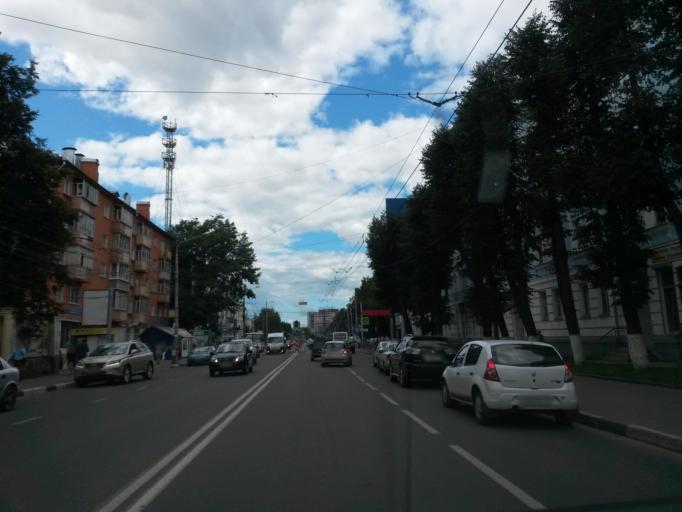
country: RU
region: Jaroslavl
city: Yaroslavl
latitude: 57.6353
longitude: 39.8693
